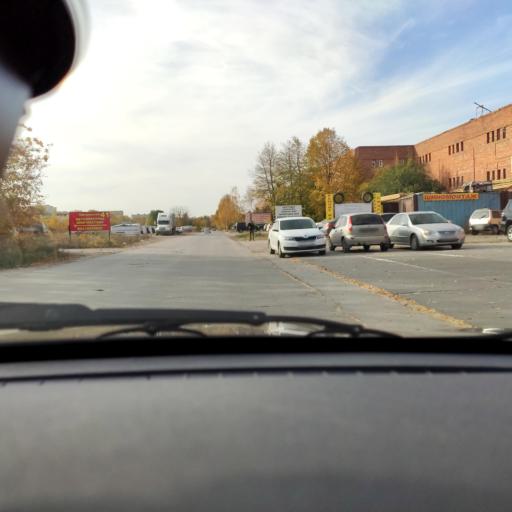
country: RU
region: Samara
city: Tol'yatti
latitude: 53.5378
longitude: 49.2967
